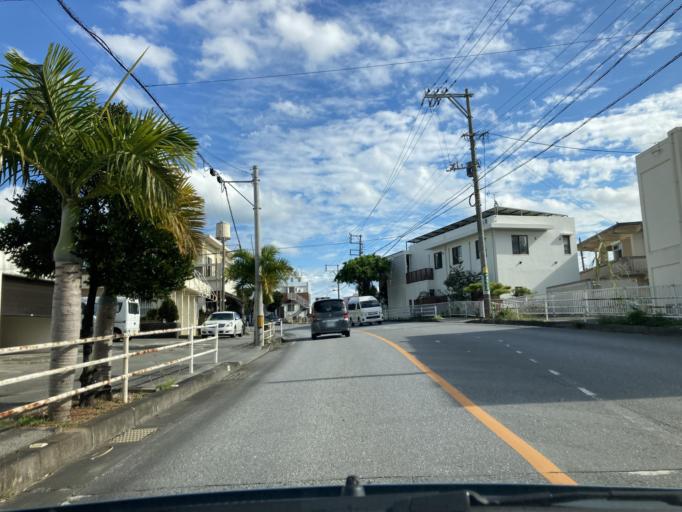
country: JP
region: Okinawa
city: Ishikawa
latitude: 26.4199
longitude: 127.8159
